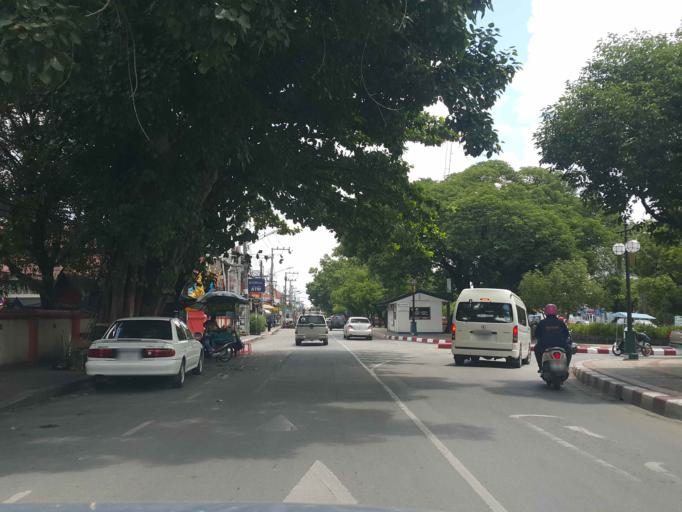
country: TH
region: Chiang Mai
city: Chiang Mai
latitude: 18.7823
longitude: 98.9928
